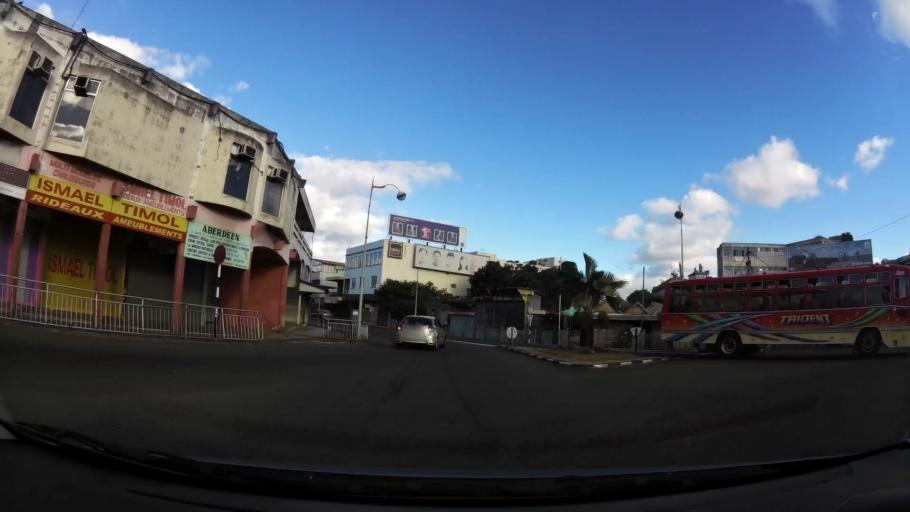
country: MU
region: Plaines Wilhems
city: Ebene
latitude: -20.2433
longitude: 57.4759
